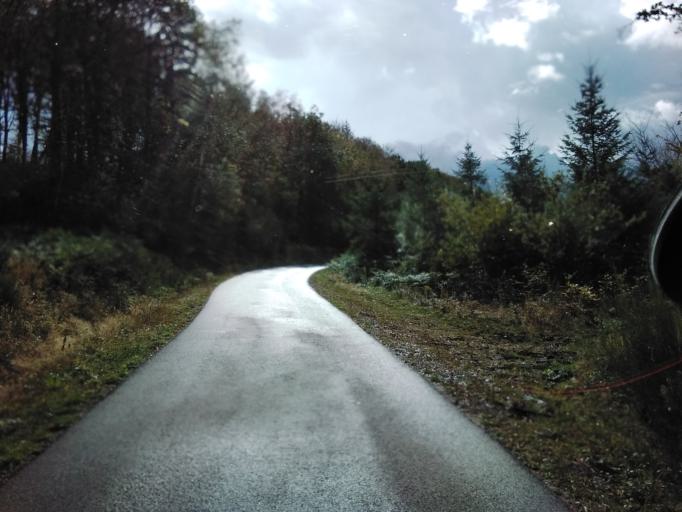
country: FR
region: Bourgogne
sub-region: Departement de la Nievre
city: Lormes
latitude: 47.3120
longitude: 3.8941
